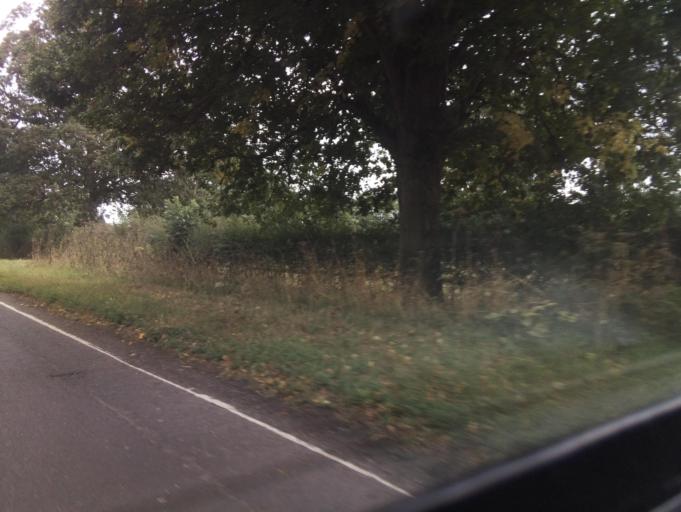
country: GB
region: England
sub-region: North Yorkshire
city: Harrogate
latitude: 54.0432
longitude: -1.5620
